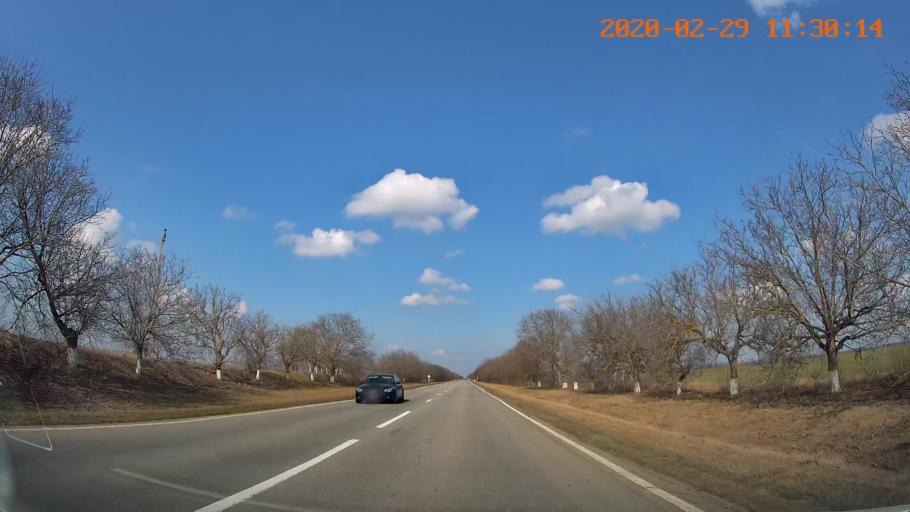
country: MD
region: Telenesti
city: Cocieri
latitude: 47.5065
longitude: 29.1174
